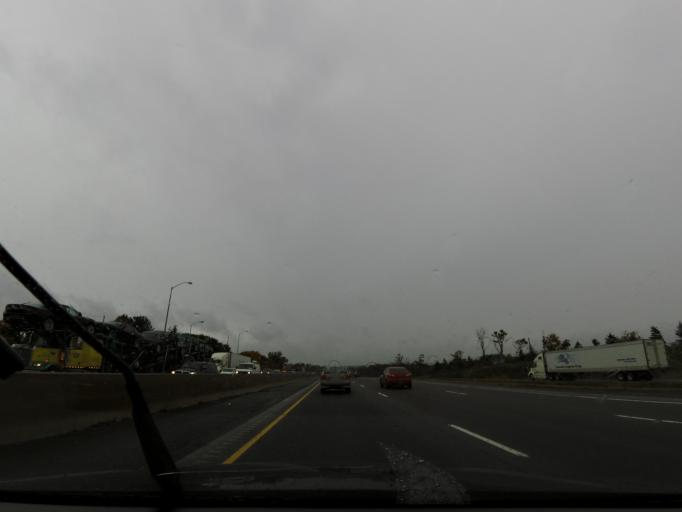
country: CA
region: Ontario
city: Cambridge
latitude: 43.4220
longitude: -80.2801
